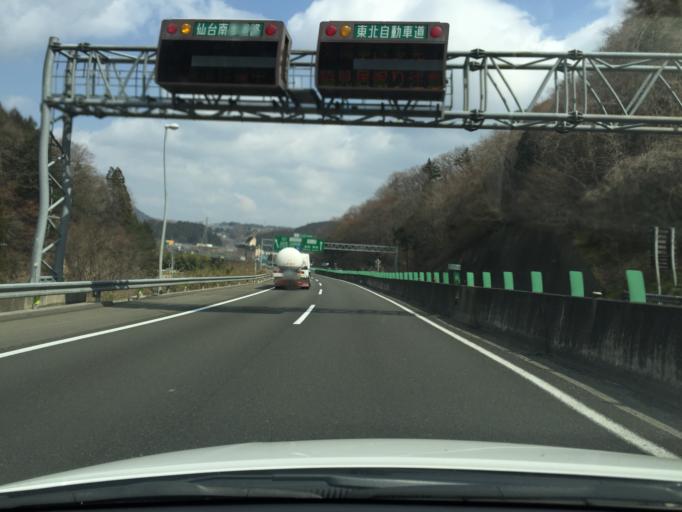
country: JP
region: Miyagi
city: Sendai
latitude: 38.2078
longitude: 140.8042
